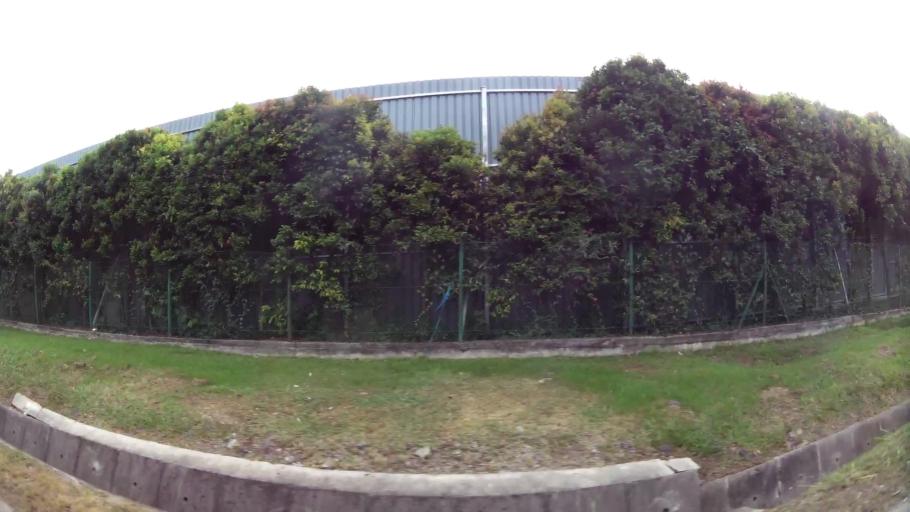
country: MY
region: Johor
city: Johor Bahru
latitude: 1.4191
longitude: 103.7092
